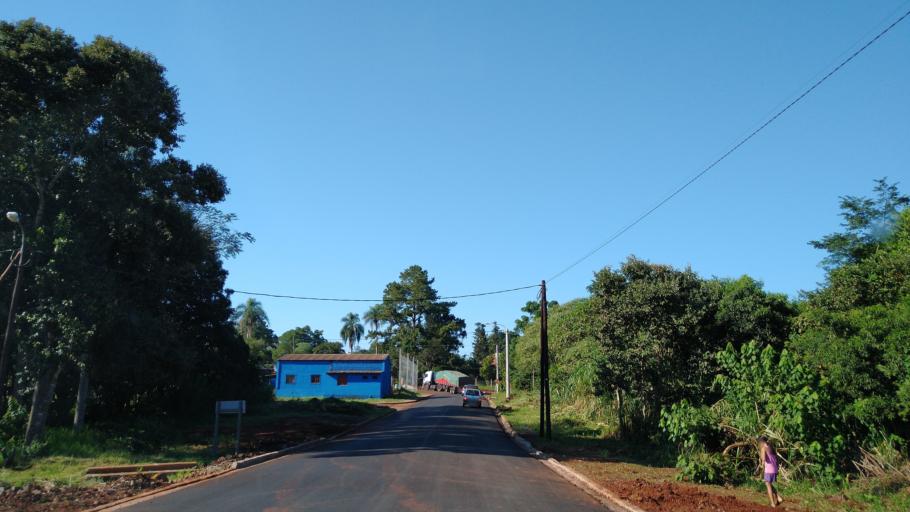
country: AR
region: Misiones
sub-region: Departamento de Montecarlo
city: Montecarlo
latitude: -26.5633
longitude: -54.7716
